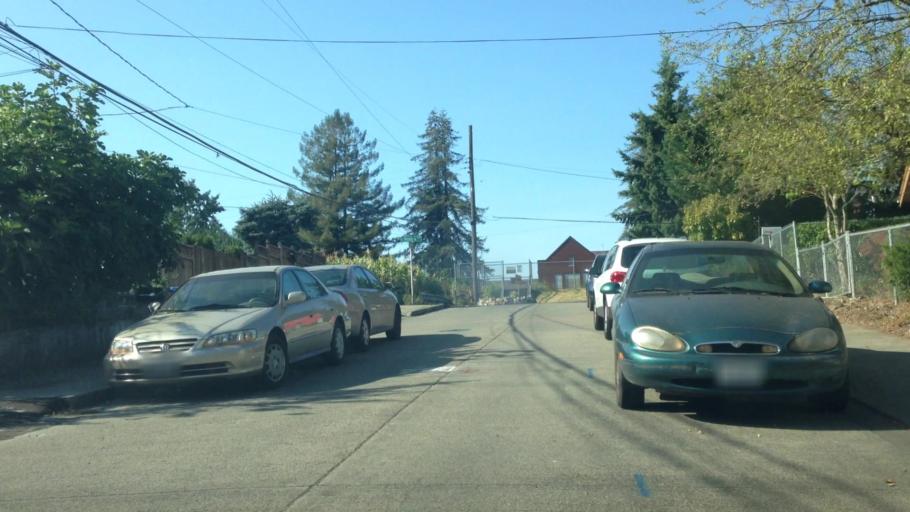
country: US
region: Washington
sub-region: King County
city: Seattle
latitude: 47.5721
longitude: -122.2910
